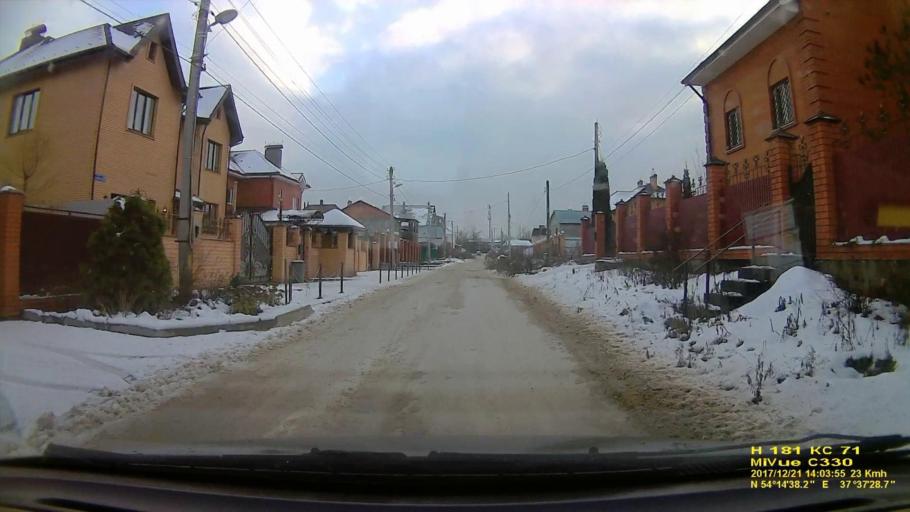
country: RU
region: Tula
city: Gorelki
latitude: 54.2439
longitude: 37.6246
